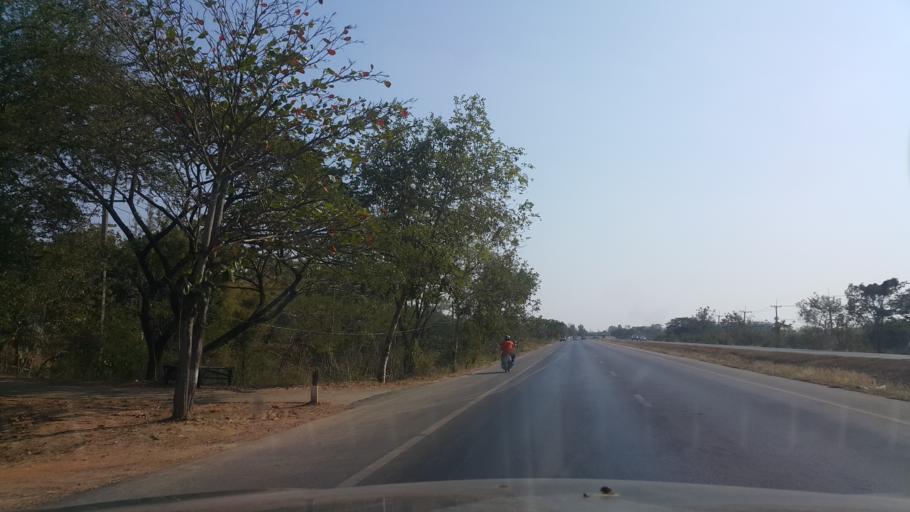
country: TH
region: Khon Kaen
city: Khon Kaen
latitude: 16.4273
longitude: 102.9174
